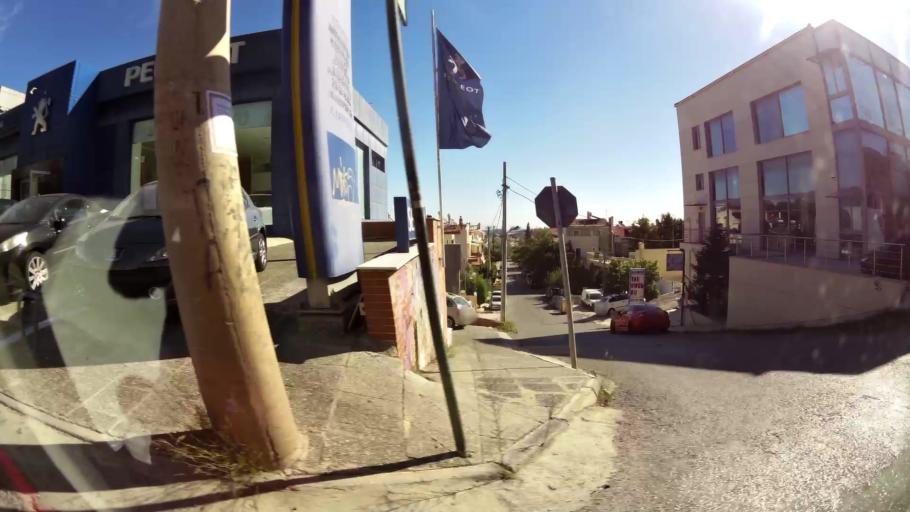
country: GR
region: Attica
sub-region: Nomarchia Anatolikis Attikis
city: Leondarion
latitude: 38.0000
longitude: 23.8479
